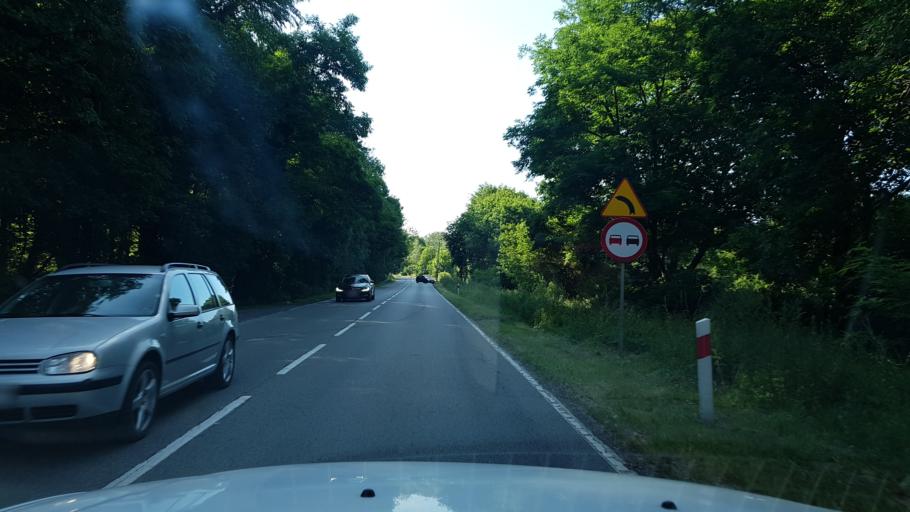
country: PL
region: West Pomeranian Voivodeship
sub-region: Powiat gryfinski
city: Stare Czarnowo
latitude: 53.3406
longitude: 14.7610
